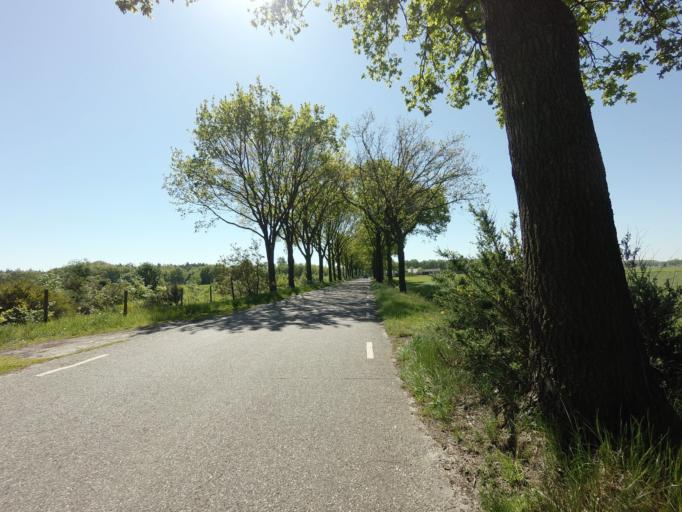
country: BE
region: Flanders
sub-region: Provincie Antwerpen
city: Essen
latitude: 51.4888
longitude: 4.4845
